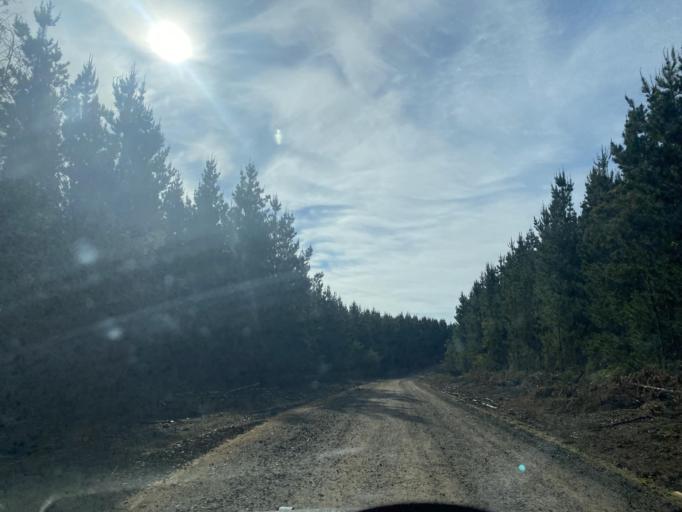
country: AU
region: Victoria
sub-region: Mansfield
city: Mansfield
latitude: -36.8769
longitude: 146.1856
